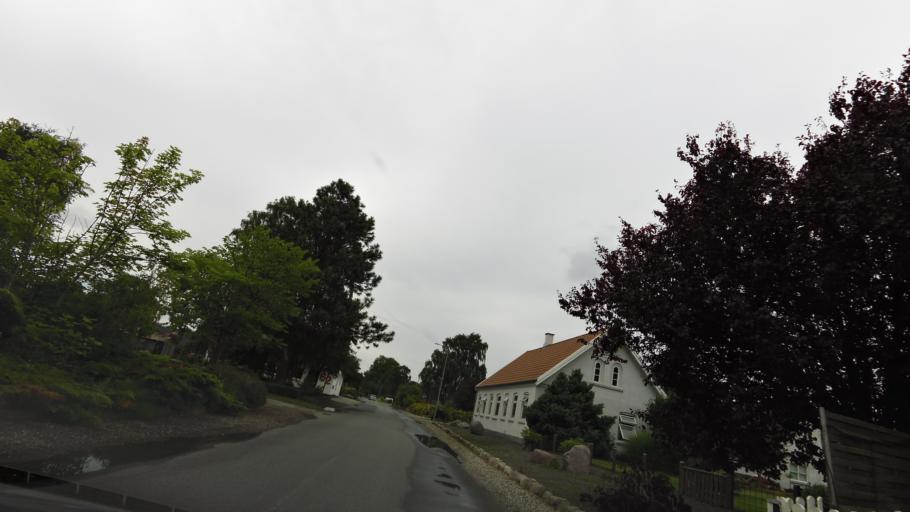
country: DK
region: South Denmark
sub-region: Nordfyns Kommune
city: Otterup
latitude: 55.5841
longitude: 10.3903
